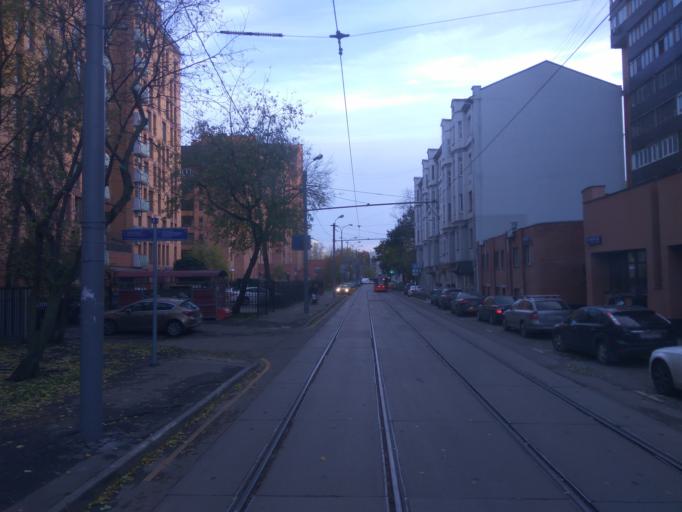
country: RU
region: Moscow
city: Mar'ina Roshcha
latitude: 55.7875
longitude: 37.6006
